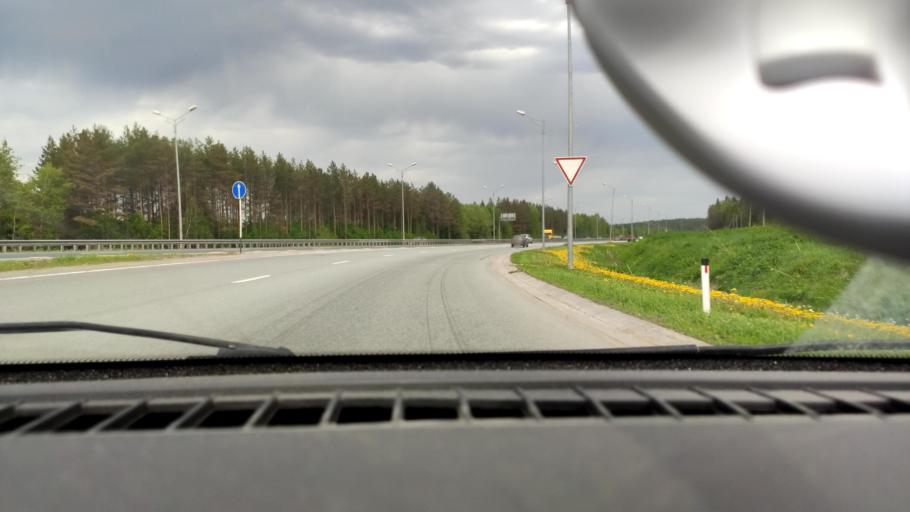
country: RU
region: Perm
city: Ferma
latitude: 58.0024
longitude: 56.3917
